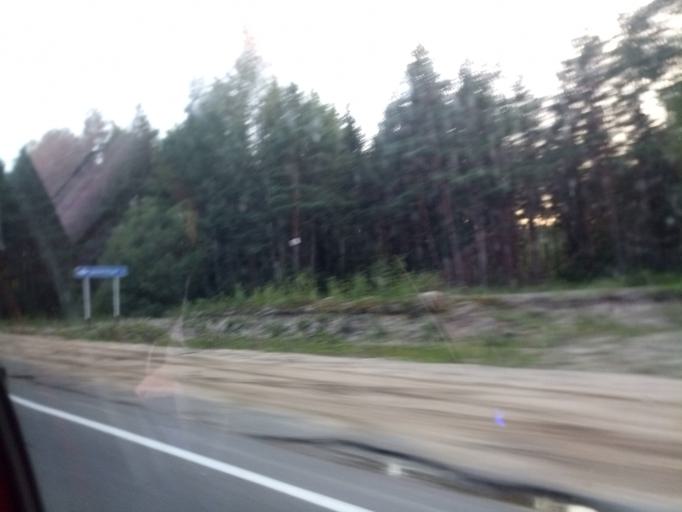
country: RU
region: Moskovskaya
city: Noginsk-9
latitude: 56.0824
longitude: 38.5764
